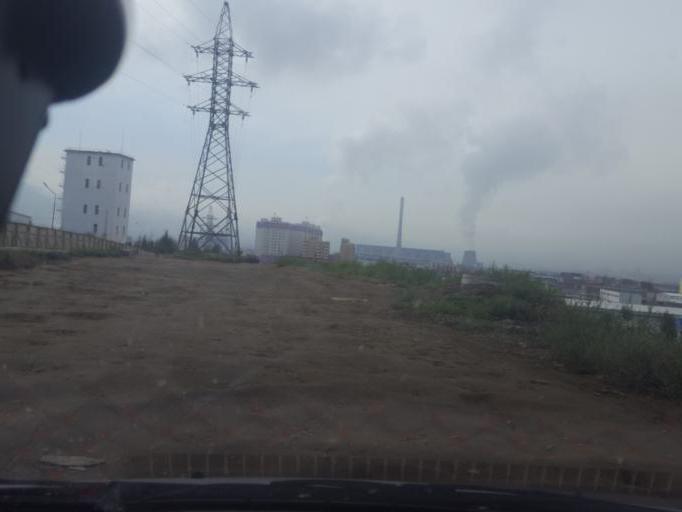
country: MN
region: Ulaanbaatar
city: Ulaanbaatar
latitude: 47.9173
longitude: 106.8002
